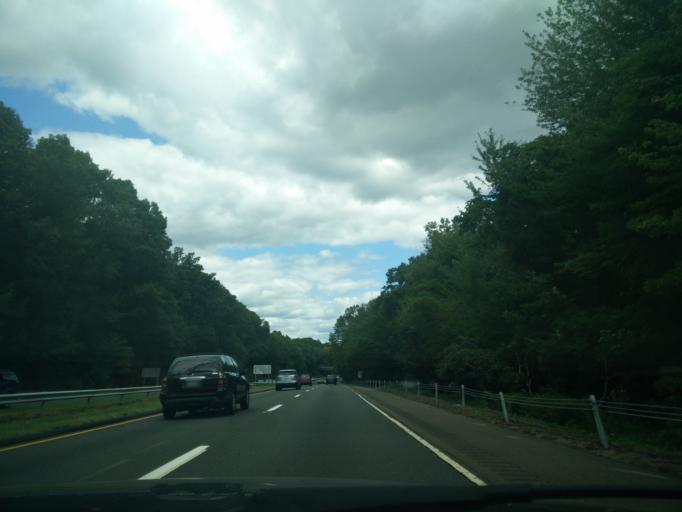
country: US
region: Connecticut
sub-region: New Haven County
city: Woodbridge
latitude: 41.3487
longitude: -72.9659
